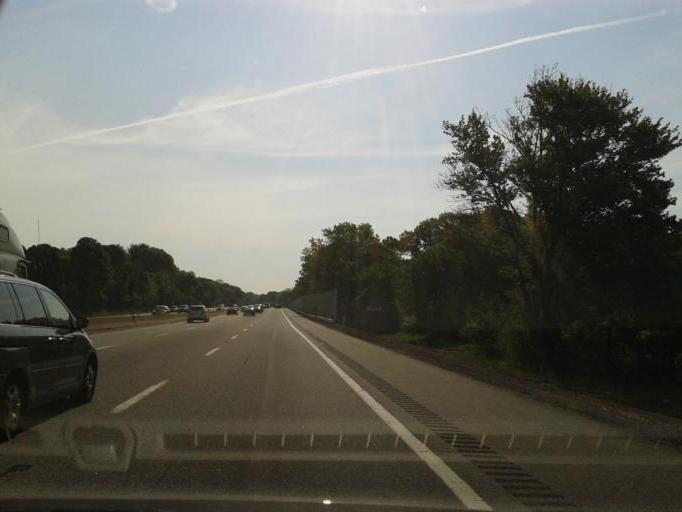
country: US
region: Massachusetts
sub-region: Middlesex County
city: Framingham Center
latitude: 42.3010
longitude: -71.4626
